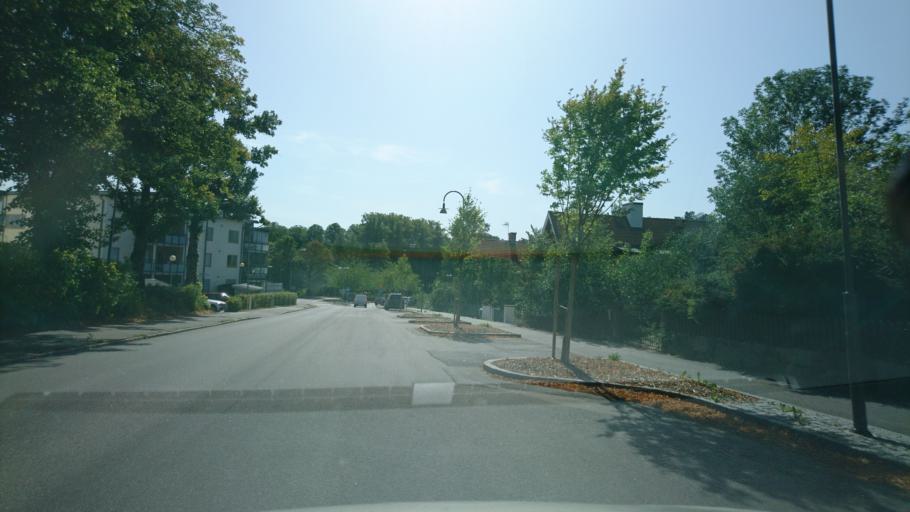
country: SE
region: Soedermanland
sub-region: Strangnas Kommun
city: Strangnas
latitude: 59.3720
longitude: 17.0314
